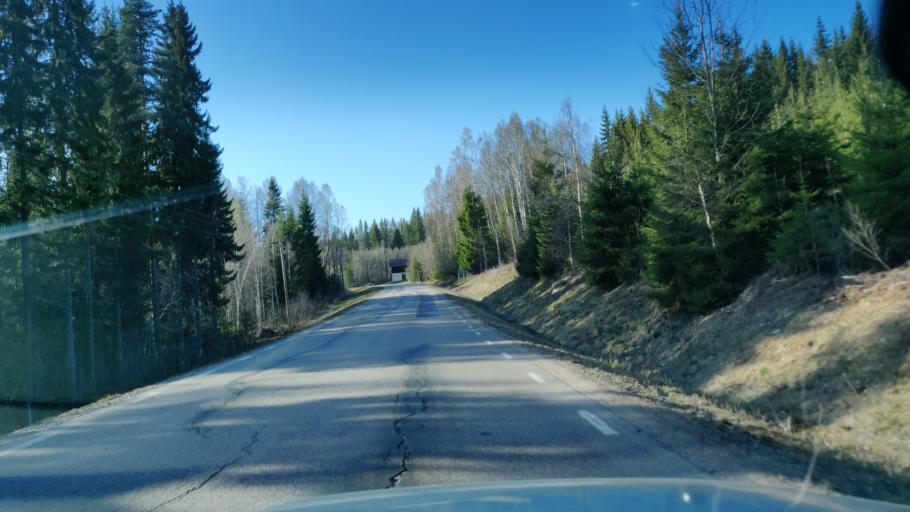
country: SE
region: Vaermland
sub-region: Munkfors Kommun
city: Munkfors
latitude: 59.9820
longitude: 13.4042
